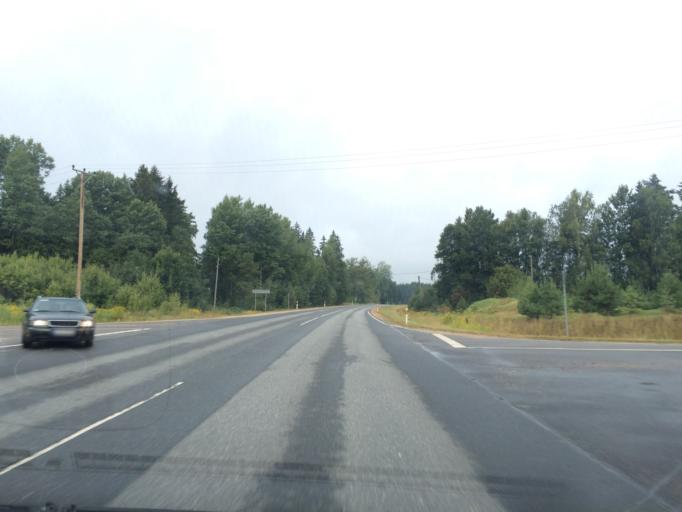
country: LV
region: Ogre
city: Ogre
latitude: 56.8561
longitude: 24.5979
